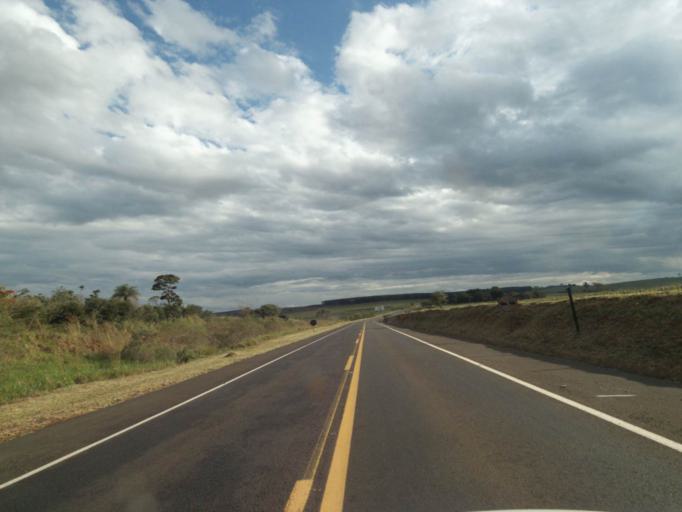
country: PY
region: Canindeyu
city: Salto del Guaira
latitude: -24.0816
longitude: -54.0661
